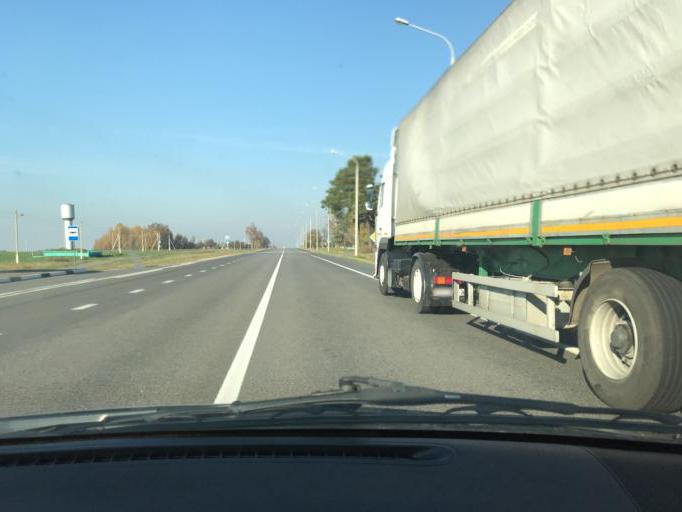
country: BY
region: Vitebsk
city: Orsha
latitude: 54.3332
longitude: 30.4464
